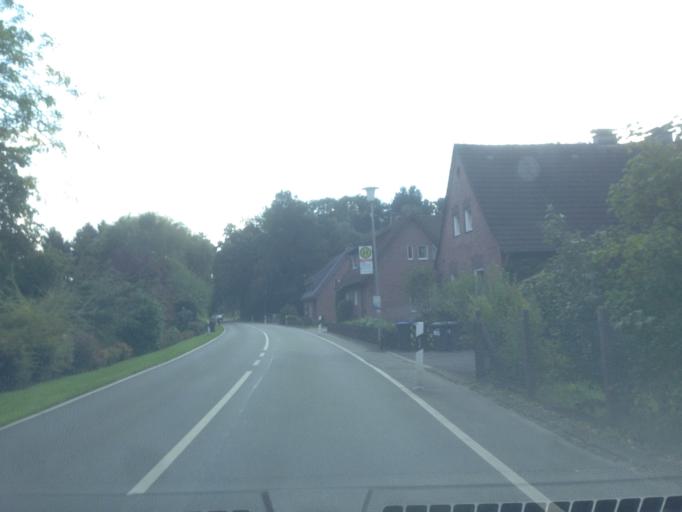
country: DE
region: North Rhine-Westphalia
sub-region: Regierungsbezirk Munster
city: Muenster
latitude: 52.0168
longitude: 7.6037
